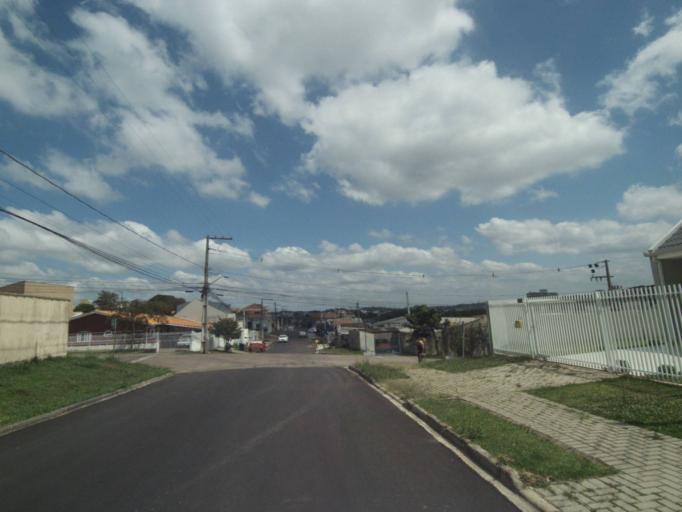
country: BR
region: Parana
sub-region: Curitiba
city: Curitiba
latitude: -25.5040
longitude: -49.3064
